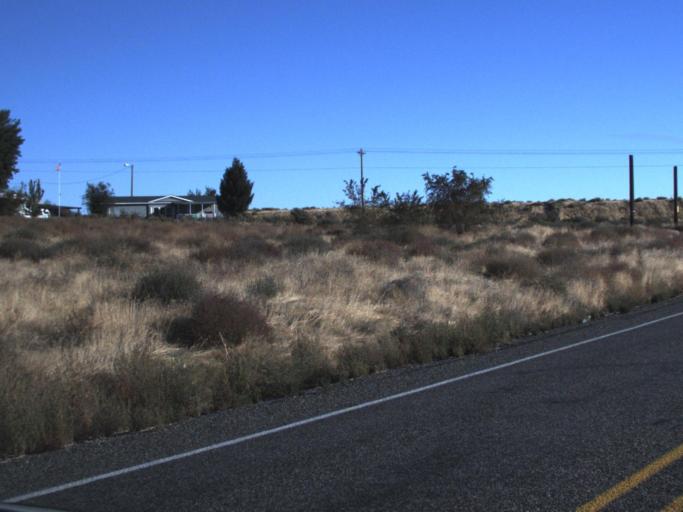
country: US
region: Washington
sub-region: Benton County
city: West Richland
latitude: 46.2840
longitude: -119.3924
